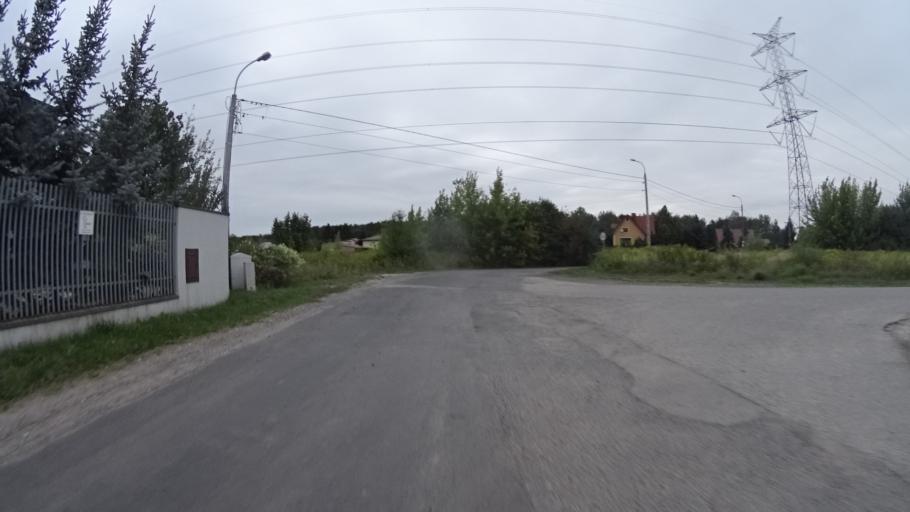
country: PL
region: Masovian Voivodeship
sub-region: Powiat warszawski zachodni
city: Stare Babice
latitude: 52.2606
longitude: 20.8195
